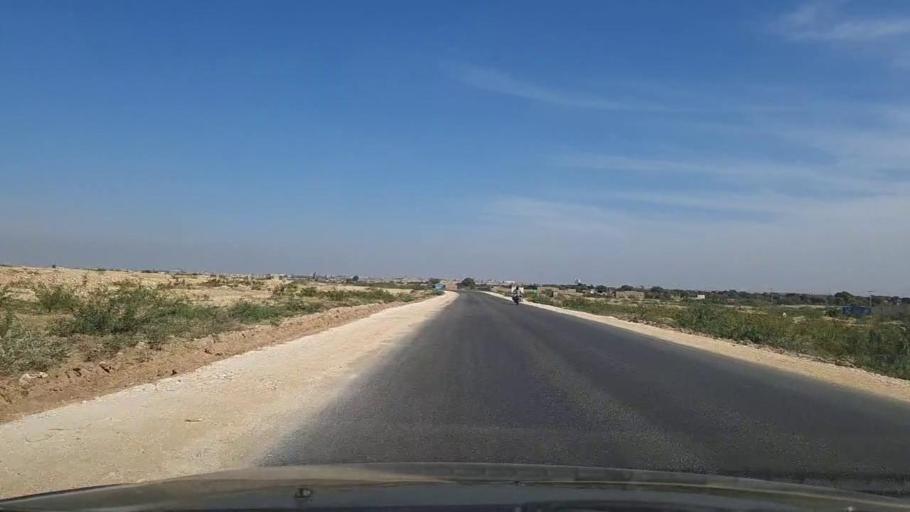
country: PK
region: Sindh
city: Kotri
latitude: 25.3186
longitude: 68.2276
